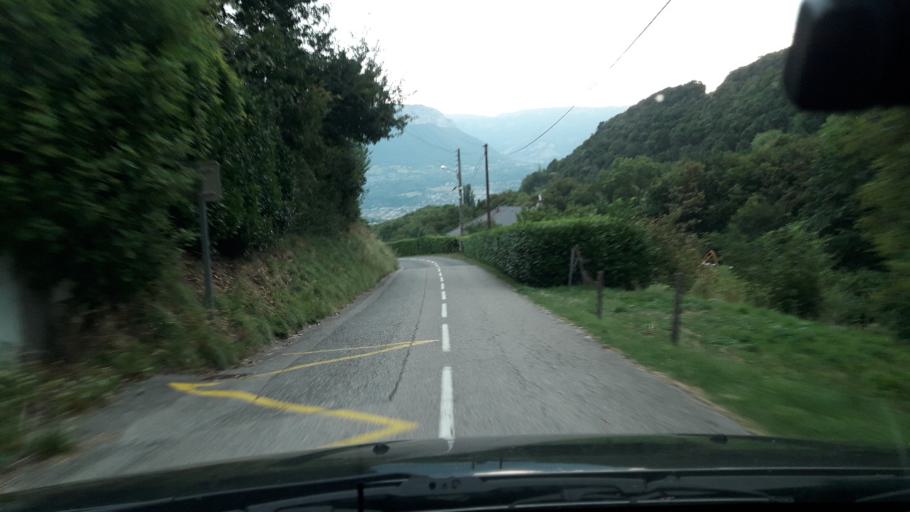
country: FR
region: Rhone-Alpes
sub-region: Departement de la Savoie
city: Barberaz
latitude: 45.5421
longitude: 5.9347
